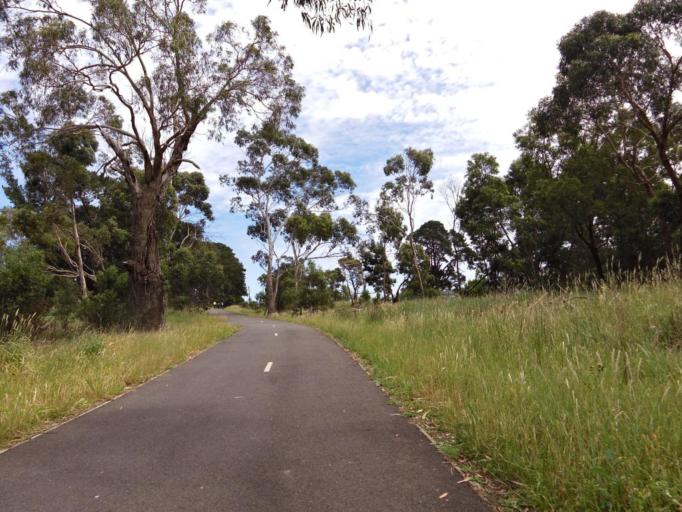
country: AU
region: Victoria
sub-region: Mornington Peninsula
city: Moorooduc
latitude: -38.2125
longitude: 145.1160
